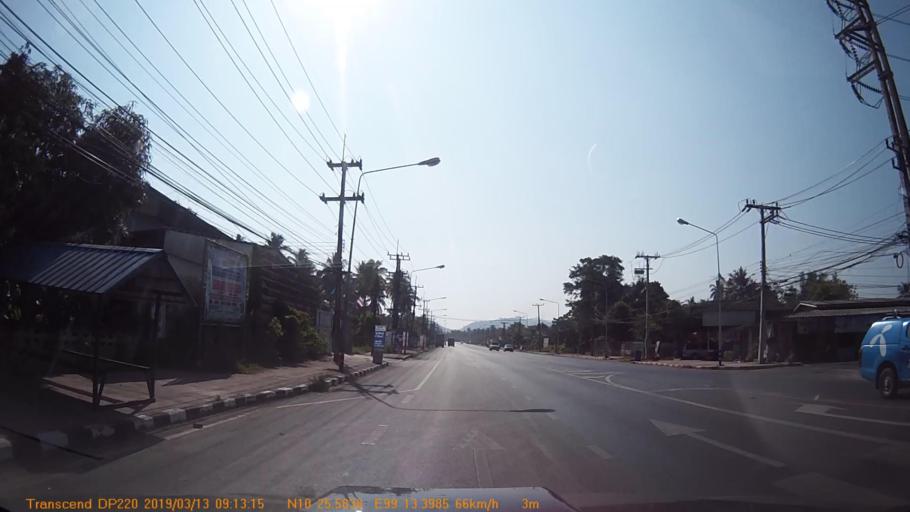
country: TH
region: Chumphon
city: Chumphon
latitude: 10.4267
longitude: 99.2233
